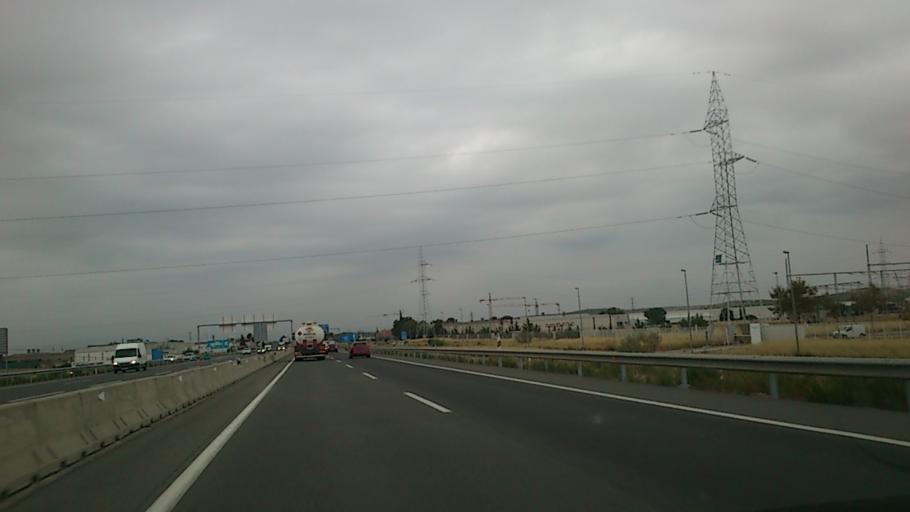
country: ES
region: Aragon
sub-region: Provincia de Zaragoza
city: Villanueva de Gallego
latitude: 41.7438
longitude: -0.8429
